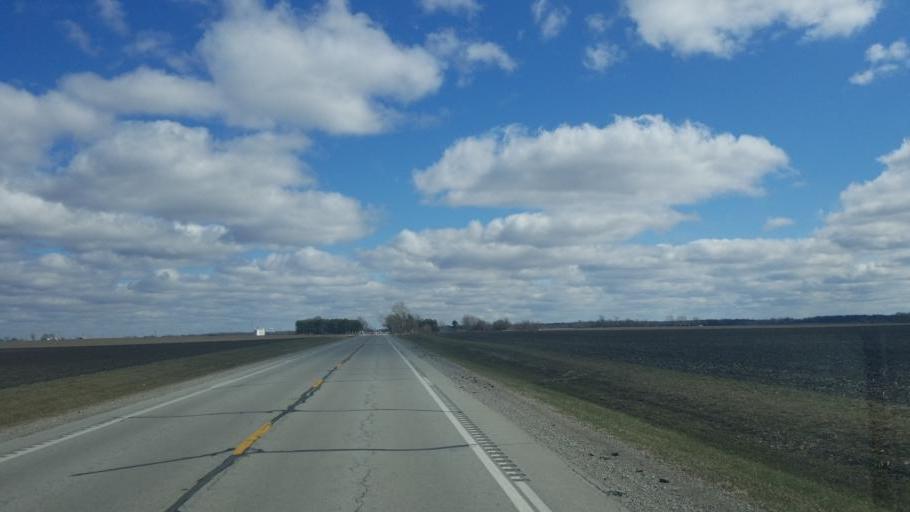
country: US
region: Illinois
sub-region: Douglas County
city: Villa Grove
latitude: 39.7921
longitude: -88.0435
